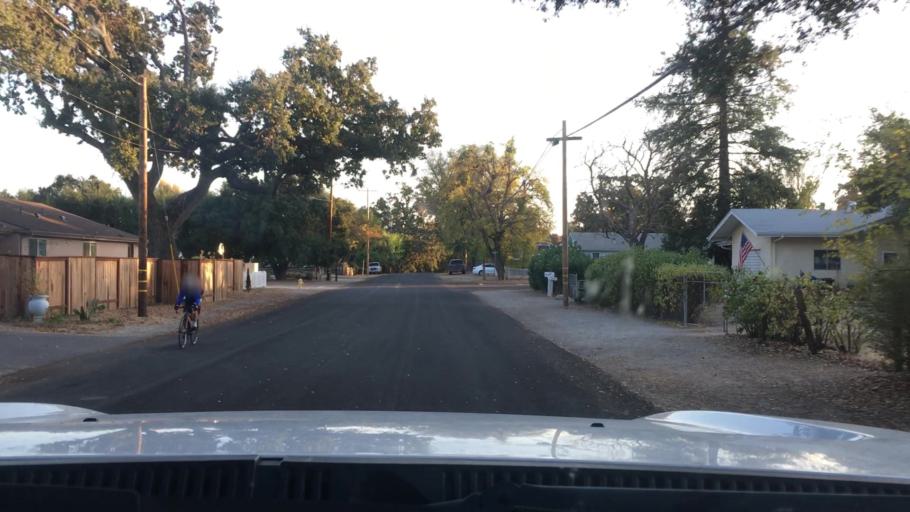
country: US
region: California
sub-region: San Luis Obispo County
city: Templeton
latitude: 35.5540
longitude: -120.7073
